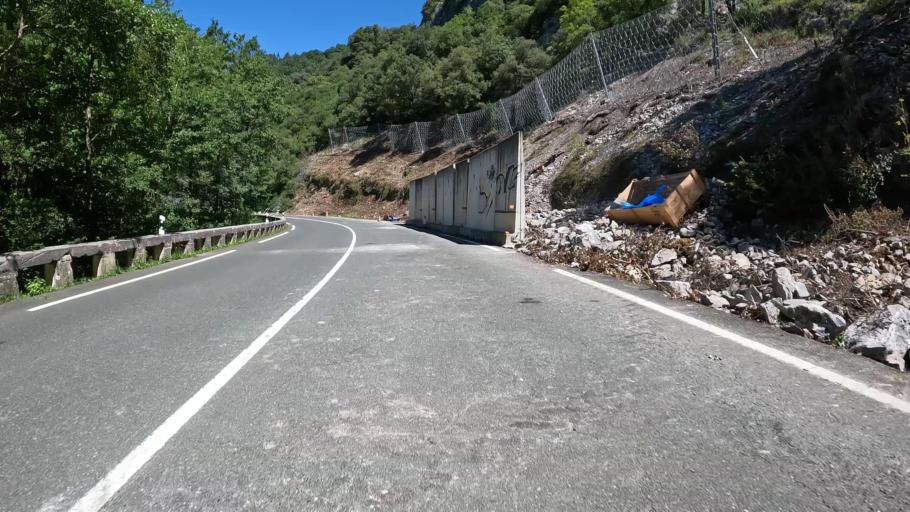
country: ES
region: Basque Country
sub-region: Provincia de Guipuzcoa
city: Oreja
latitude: 43.0785
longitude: -2.0175
